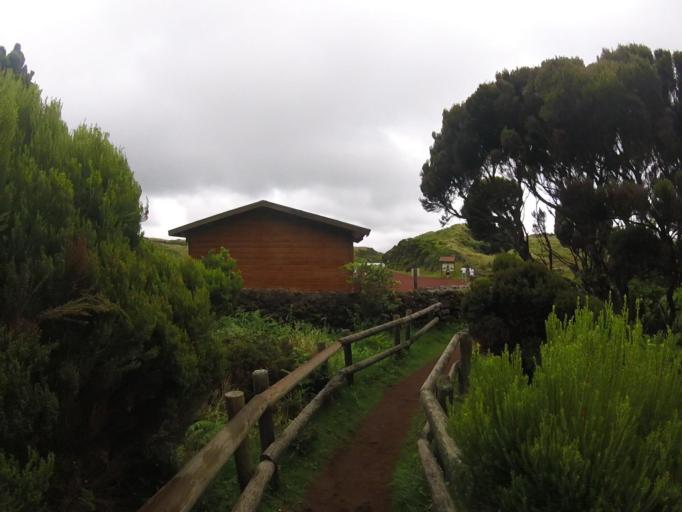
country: PT
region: Azores
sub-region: Praia da Vitoria
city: Biscoitos
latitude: 38.7292
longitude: -27.2307
